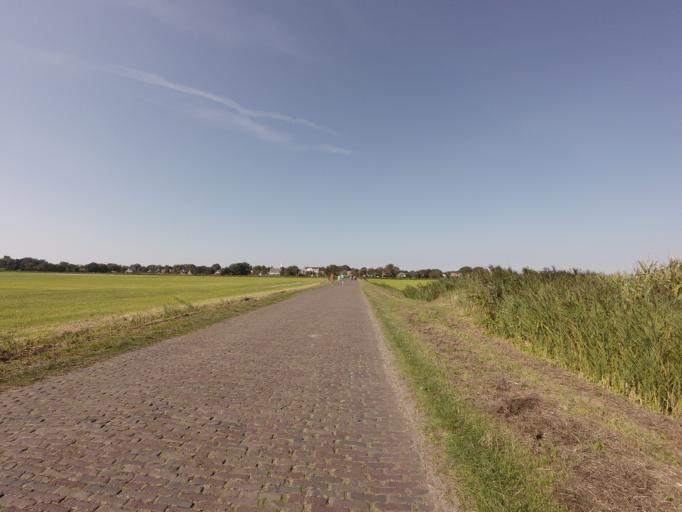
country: NL
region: Friesland
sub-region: Gemeente Schiermonnikoog
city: Schiermonnikoog
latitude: 53.4735
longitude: 6.1616
